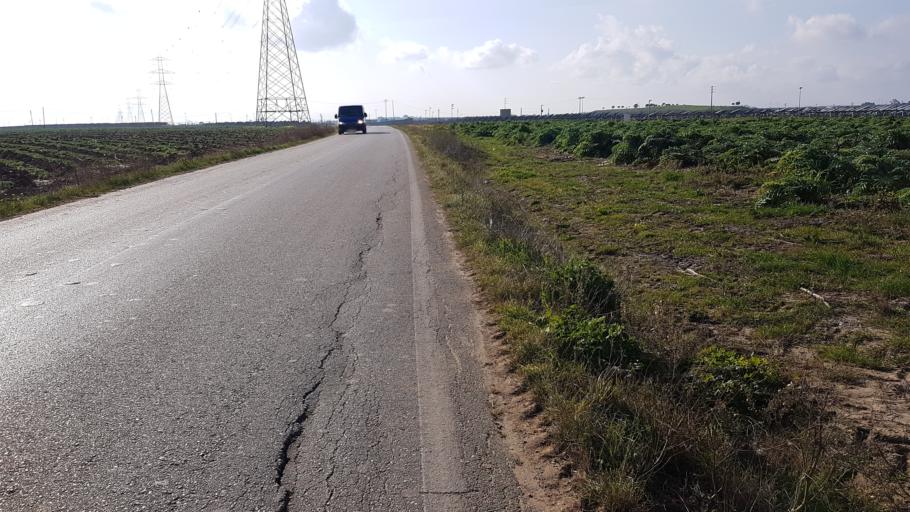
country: IT
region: Apulia
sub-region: Provincia di Brindisi
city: La Rosa
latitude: 40.5924
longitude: 17.9034
